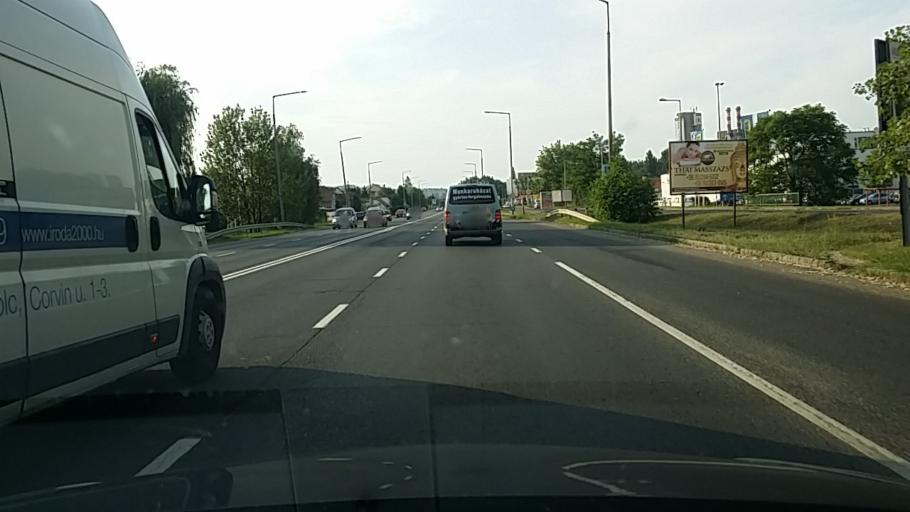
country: HU
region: Borsod-Abauj-Zemplen
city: Miskolc
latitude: 48.0568
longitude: 20.7973
